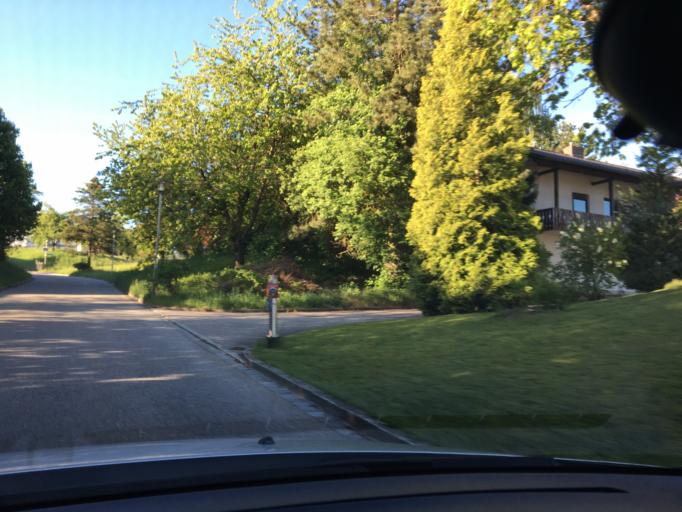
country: DE
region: Bavaria
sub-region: Lower Bavaria
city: Schalkham
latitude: 48.4956
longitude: 12.3748
